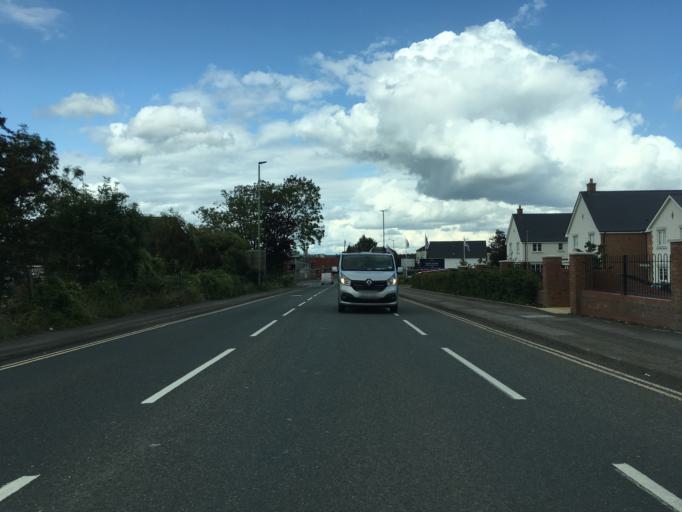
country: GB
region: England
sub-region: Gloucestershire
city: Gloucester
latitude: 51.8480
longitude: -2.2602
